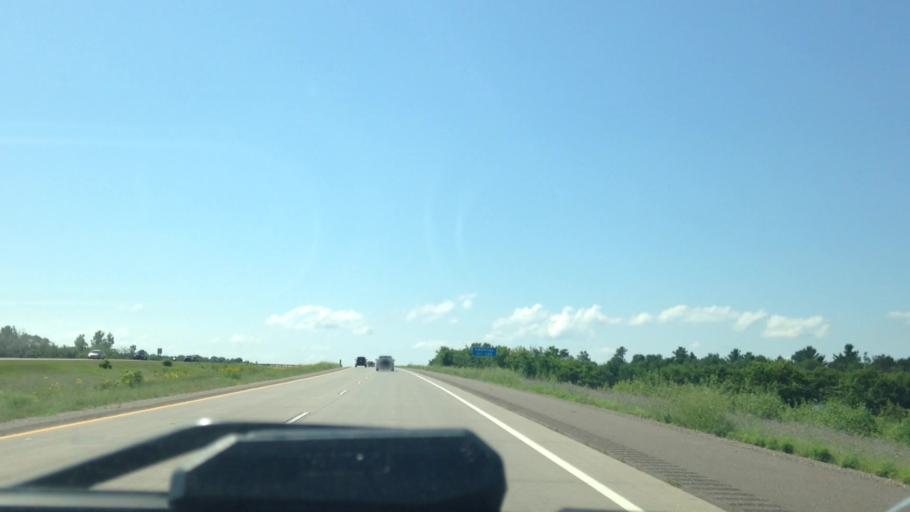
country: US
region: Wisconsin
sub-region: Barron County
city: Cameron
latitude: 45.4111
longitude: -91.7638
